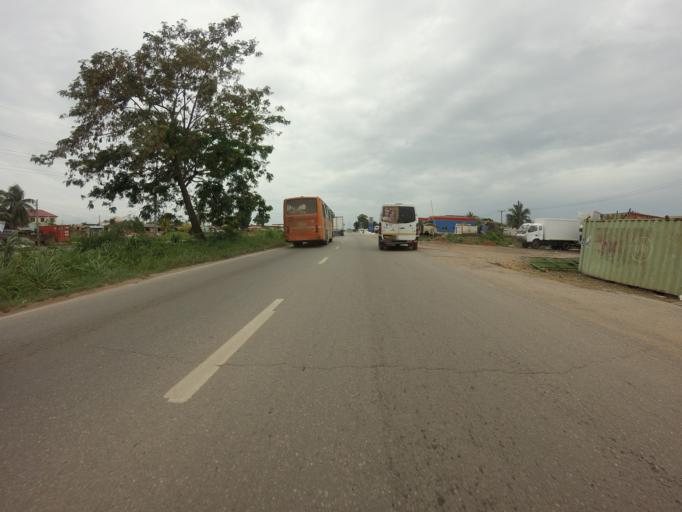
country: GH
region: Greater Accra
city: Achiaman
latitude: 5.7093
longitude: -0.3013
